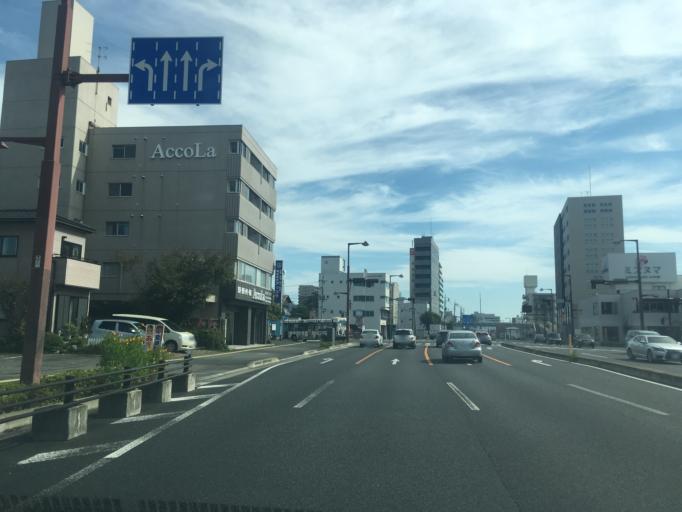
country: JP
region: Gunma
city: Maebashi-shi
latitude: 36.3875
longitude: 139.0614
